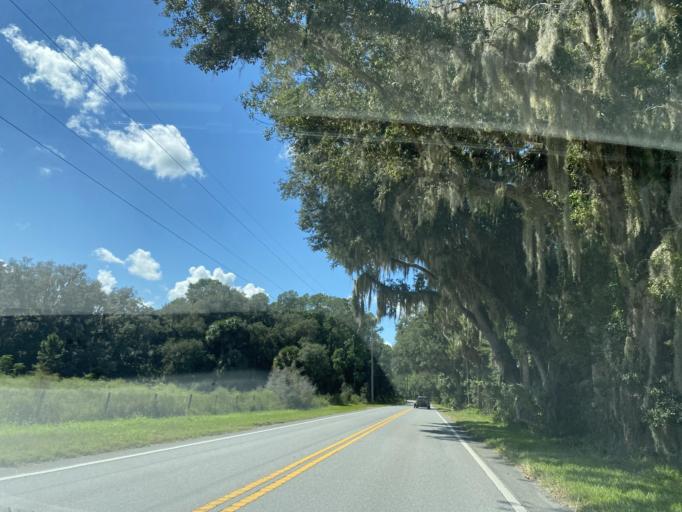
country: US
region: Florida
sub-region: Lake County
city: Umatilla
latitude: 28.9630
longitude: -81.5710
